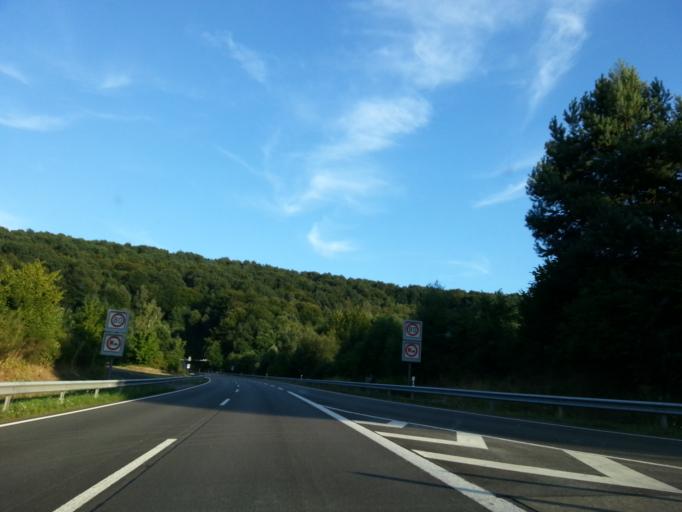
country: DE
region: Rheinland-Pfalz
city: Landstuhl
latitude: 49.3964
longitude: 7.5563
